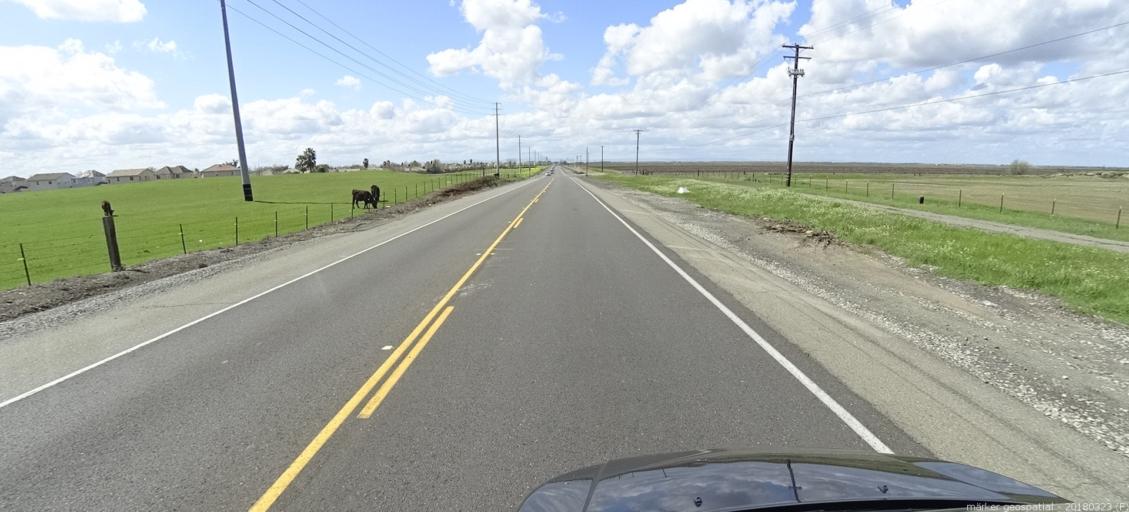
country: US
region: California
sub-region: Sacramento County
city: Elverta
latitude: 38.6852
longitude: -121.4916
